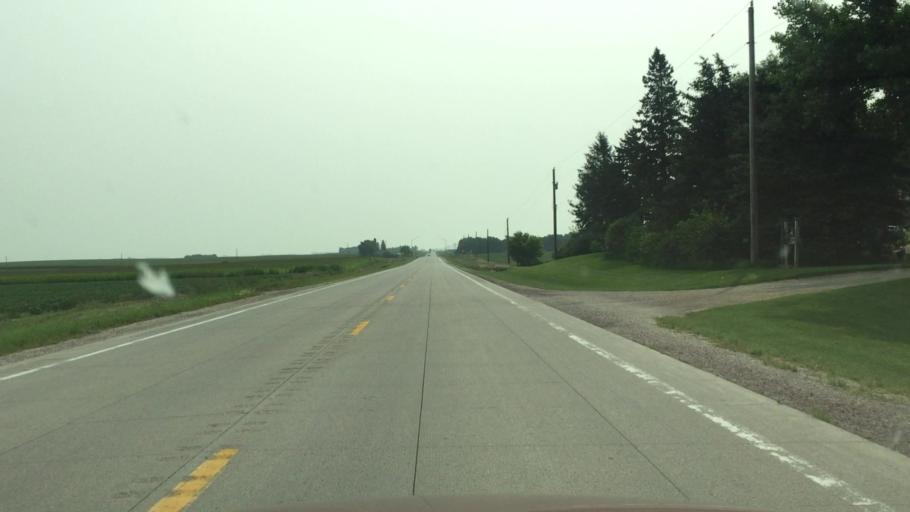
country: US
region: Iowa
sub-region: Osceola County
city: Sibley
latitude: 43.4327
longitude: -95.6501
